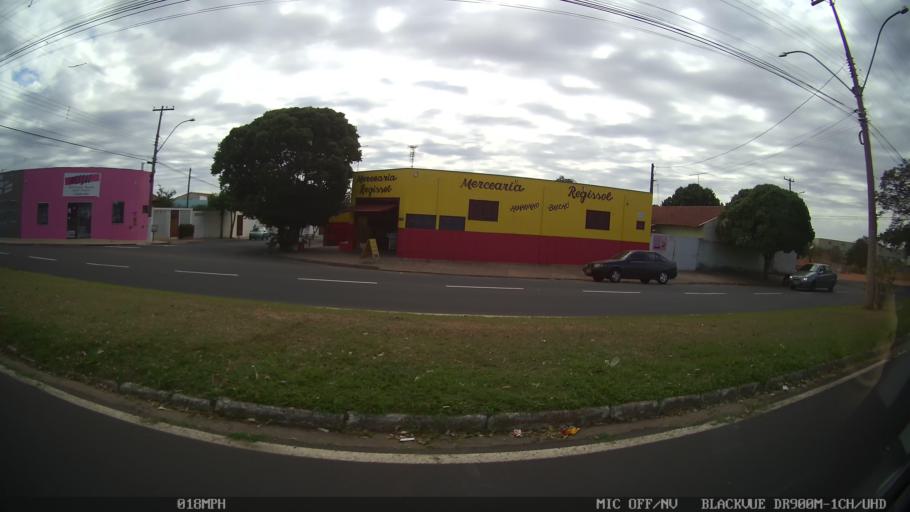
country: BR
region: Sao Paulo
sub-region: Sao Jose Do Rio Preto
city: Sao Jose do Rio Preto
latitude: -20.8051
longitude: -49.4918
